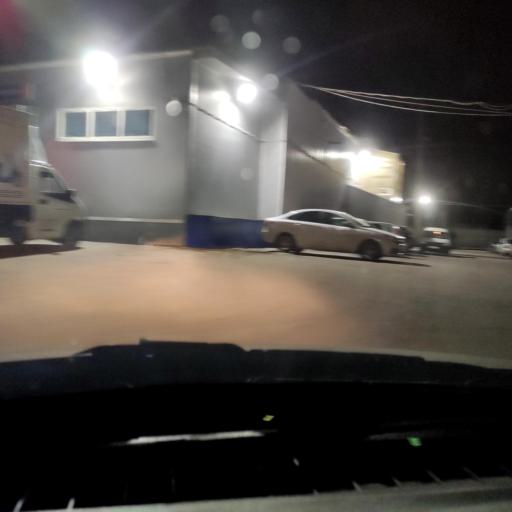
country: RU
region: Samara
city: Tol'yatti
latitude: 53.5254
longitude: 49.4689
